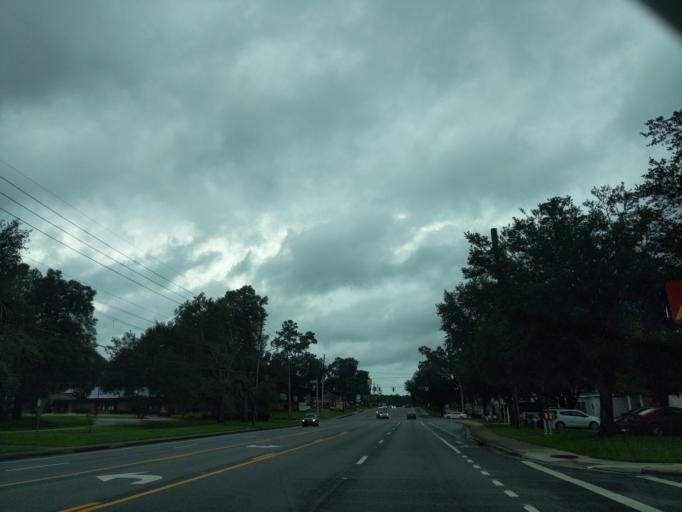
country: US
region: Florida
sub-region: Alachua County
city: Alachua
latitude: 29.6551
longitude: -82.4223
